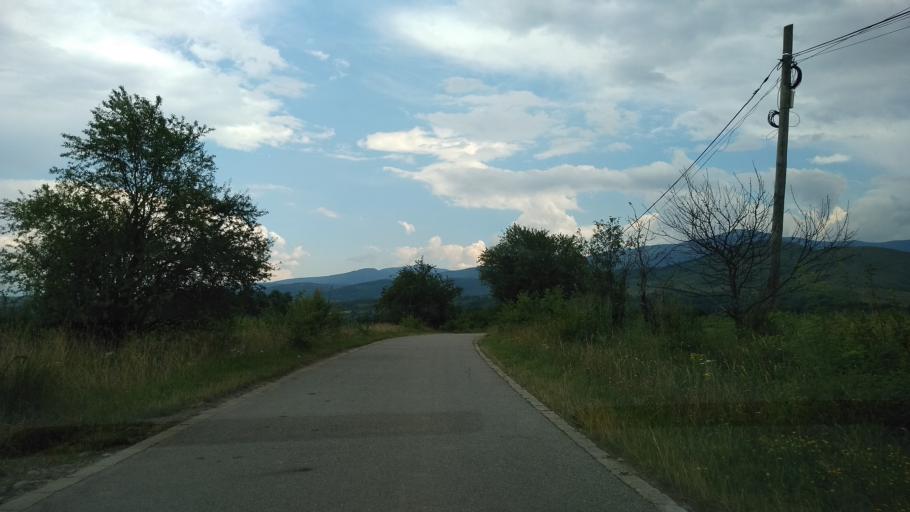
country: RO
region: Hunedoara
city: Salasu de Sus
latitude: 45.5017
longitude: 22.9661
